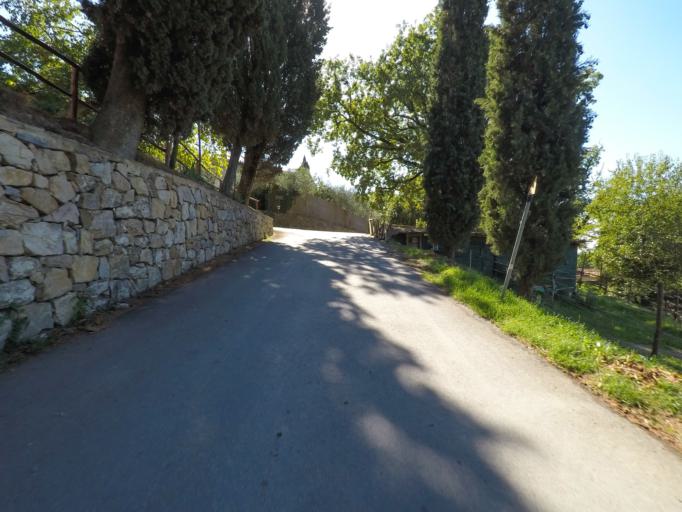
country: IT
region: Tuscany
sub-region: Provincia di Siena
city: Castellina in Chianti
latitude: 43.4356
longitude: 11.3051
